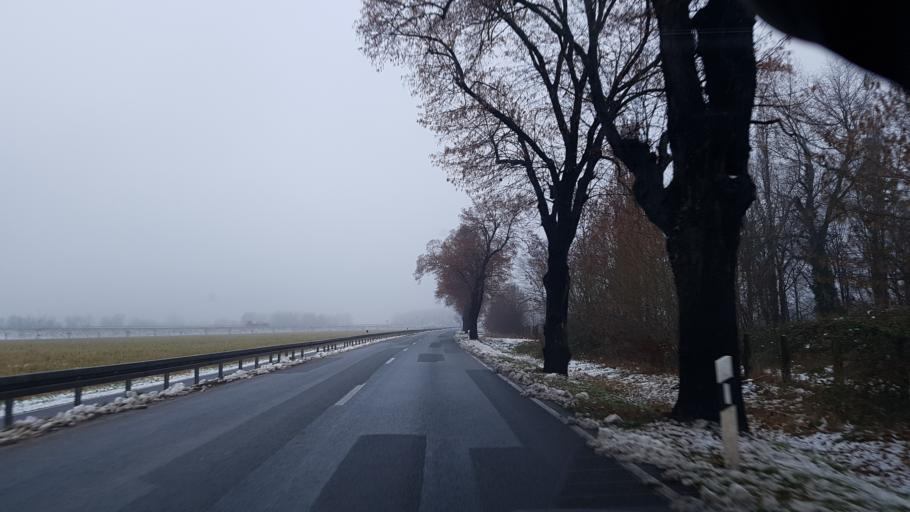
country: DE
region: Brandenburg
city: Bad Liebenwerda
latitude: 51.5143
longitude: 13.3791
